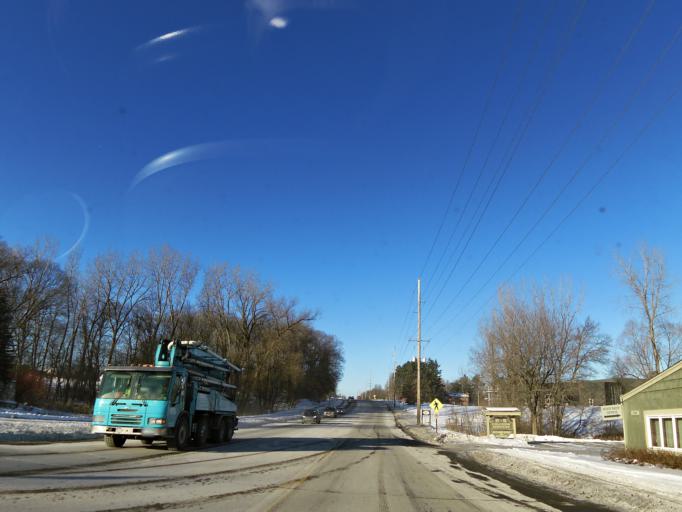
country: US
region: Minnesota
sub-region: Hennepin County
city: Mound
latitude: 44.9495
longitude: -93.6656
